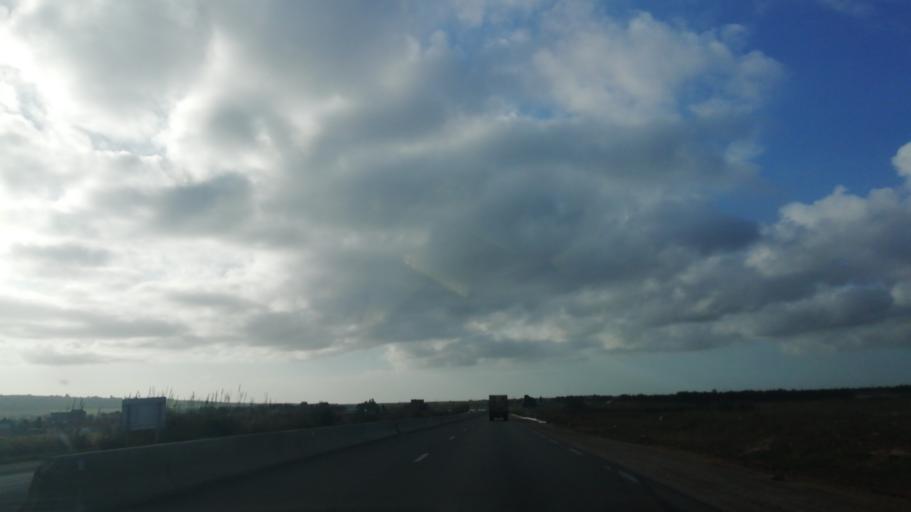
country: DZ
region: Mostaganem
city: Mostaganem
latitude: 36.1045
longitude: 0.2650
